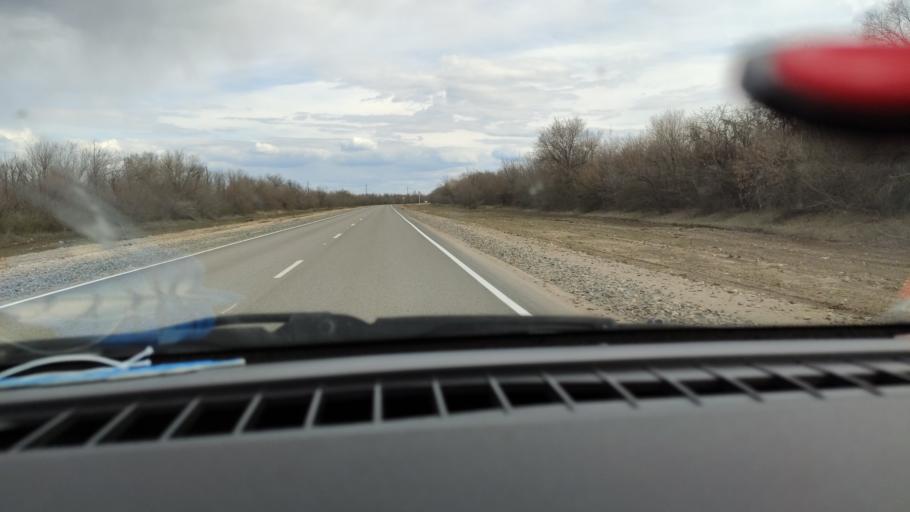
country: RU
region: Saratov
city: Privolzhskiy
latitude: 51.1575
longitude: 45.9611
